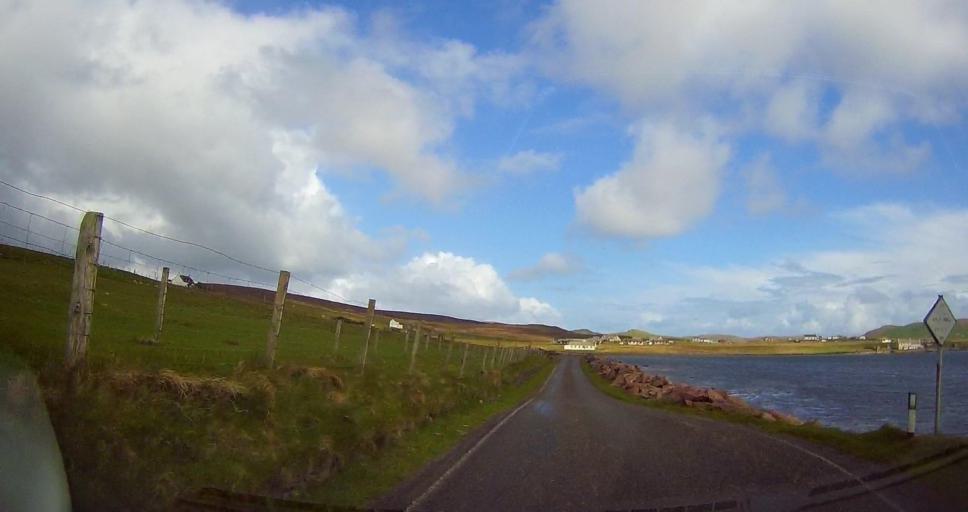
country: GB
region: Scotland
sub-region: Shetland Islands
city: Lerwick
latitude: 60.5808
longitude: -1.3334
